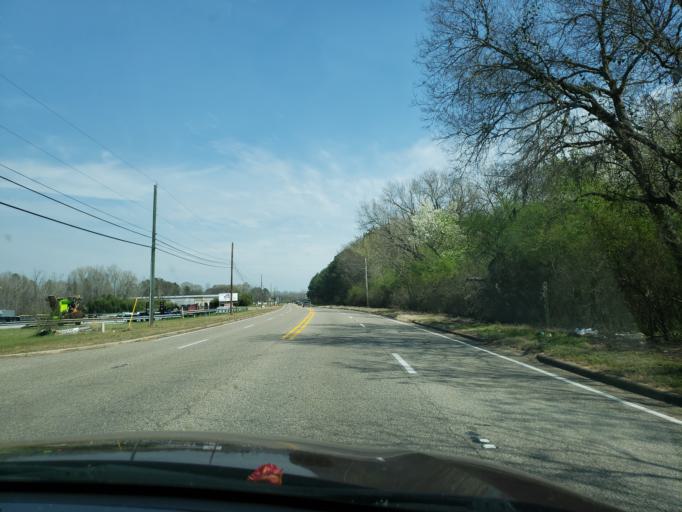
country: US
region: Alabama
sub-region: Elmore County
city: Wetumpka
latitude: 32.5353
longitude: -86.2327
